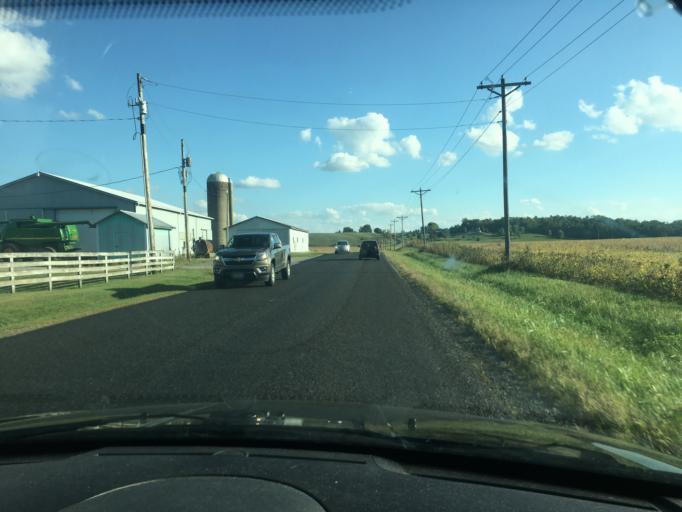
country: US
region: Ohio
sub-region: Logan County
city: West Liberty
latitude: 40.2794
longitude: -83.7253
